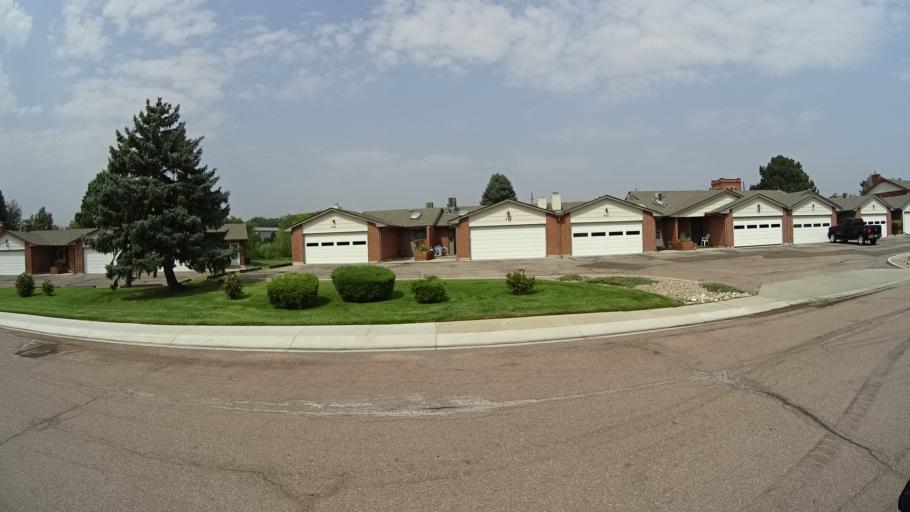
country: US
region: Colorado
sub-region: El Paso County
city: Stratmoor
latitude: 38.8239
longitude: -104.7599
